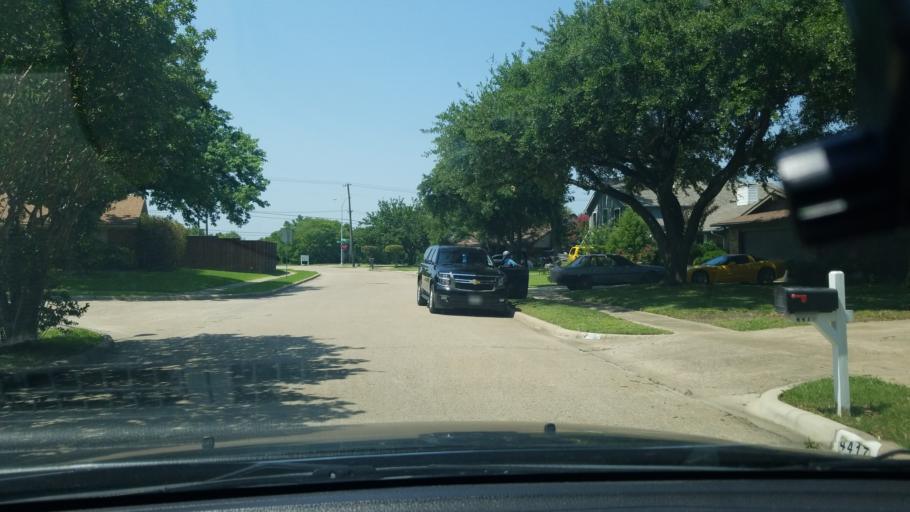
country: US
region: Texas
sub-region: Dallas County
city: Sunnyvale
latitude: 32.8254
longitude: -96.6068
